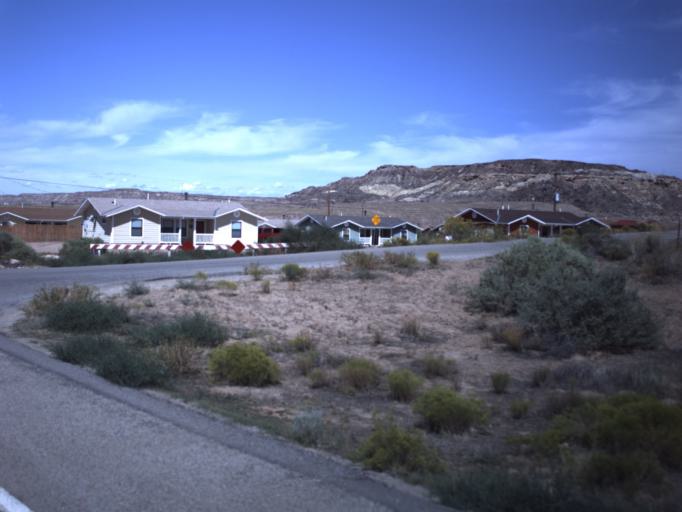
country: US
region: Colorado
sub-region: Montezuma County
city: Towaoc
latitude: 37.2150
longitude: -109.1826
